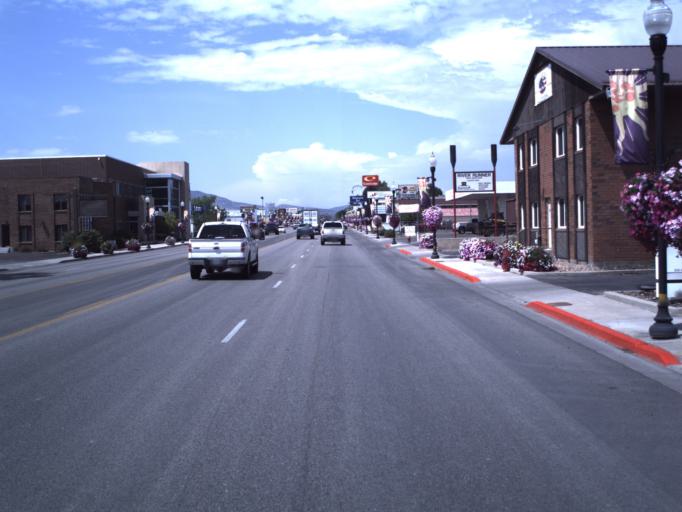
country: US
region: Utah
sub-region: Uintah County
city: Vernal
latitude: 40.4559
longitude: -109.5200
